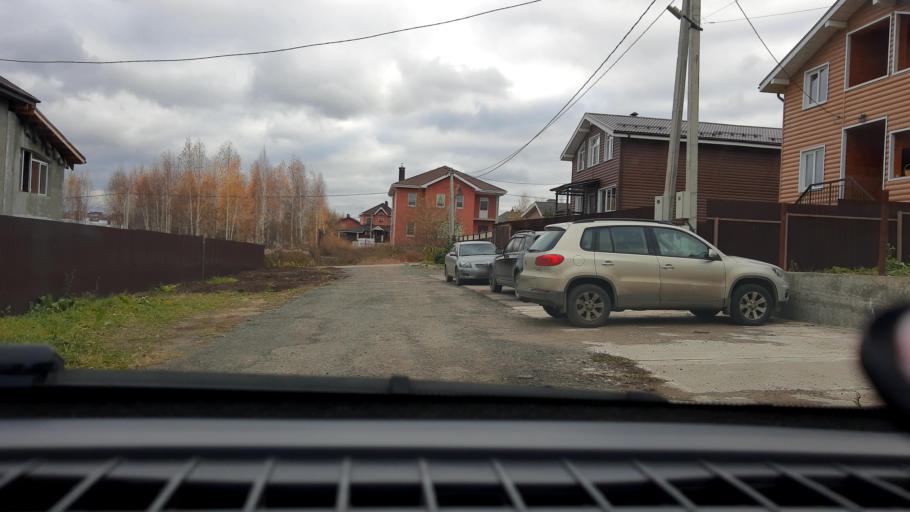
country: RU
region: Nizjnij Novgorod
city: Afonino
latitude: 56.2652
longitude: 44.0689
